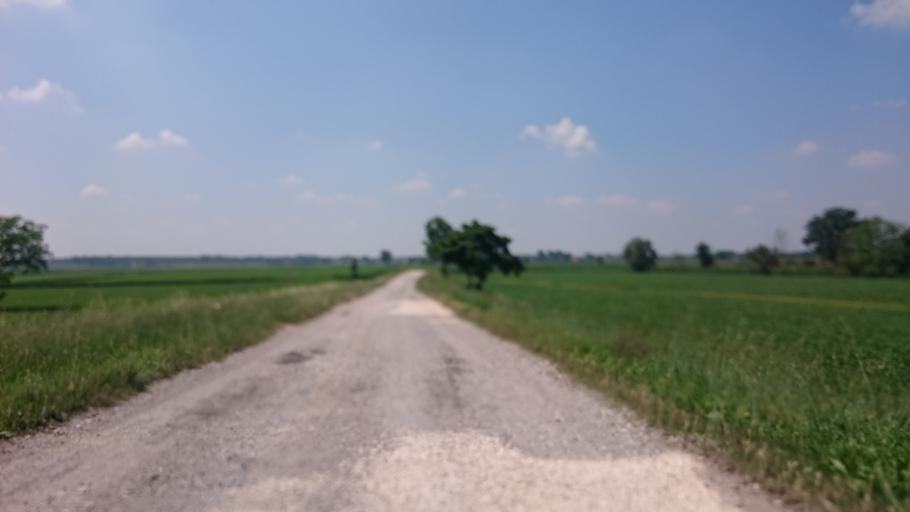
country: IT
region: Lombardy
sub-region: Provincia di Mantova
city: Roncoferraro
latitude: 45.0939
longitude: 10.9283
